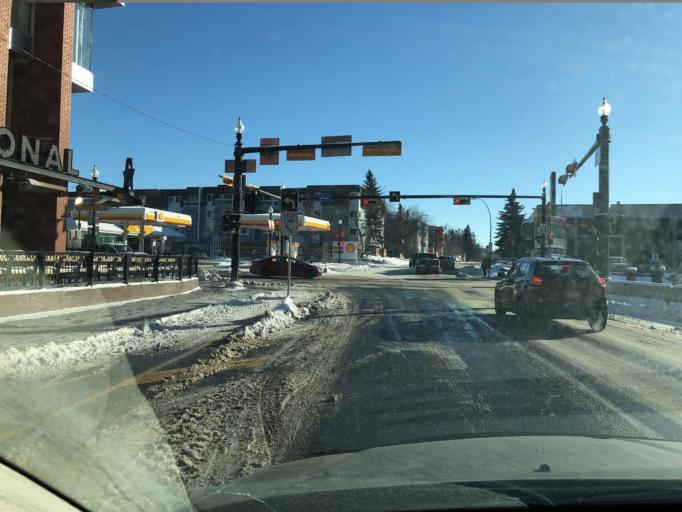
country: CA
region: Alberta
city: Calgary
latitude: 51.0382
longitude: -114.0743
